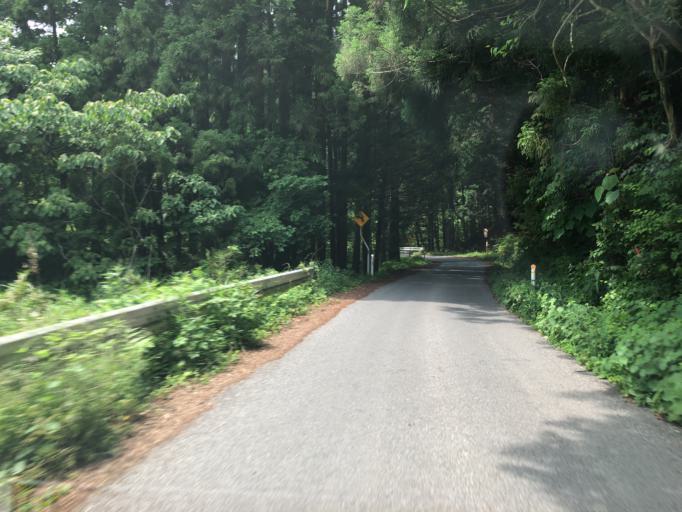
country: JP
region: Miyagi
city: Marumori
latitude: 37.8291
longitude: 140.8642
